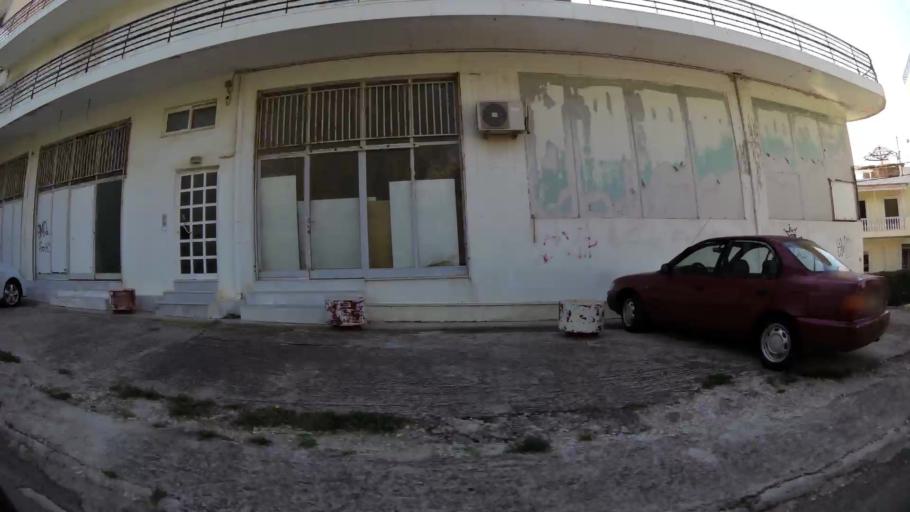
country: GR
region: Attica
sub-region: Nomarchia Athinas
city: Argyroupoli
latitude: 37.9107
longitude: 23.7586
